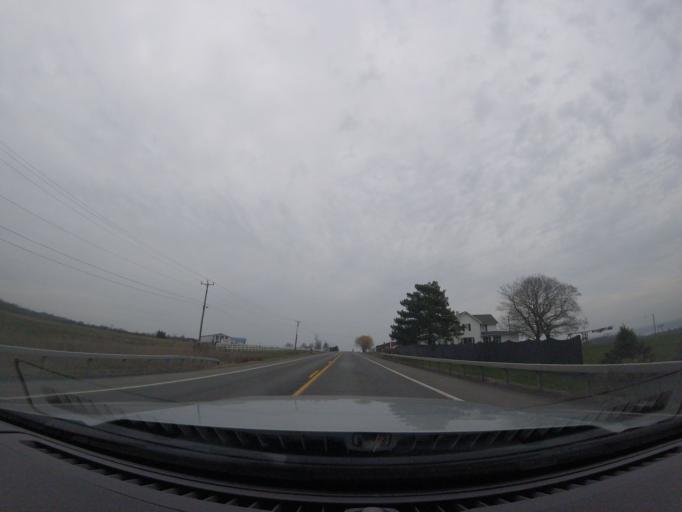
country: US
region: New York
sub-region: Yates County
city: Dundee
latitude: 42.6273
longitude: -76.9438
